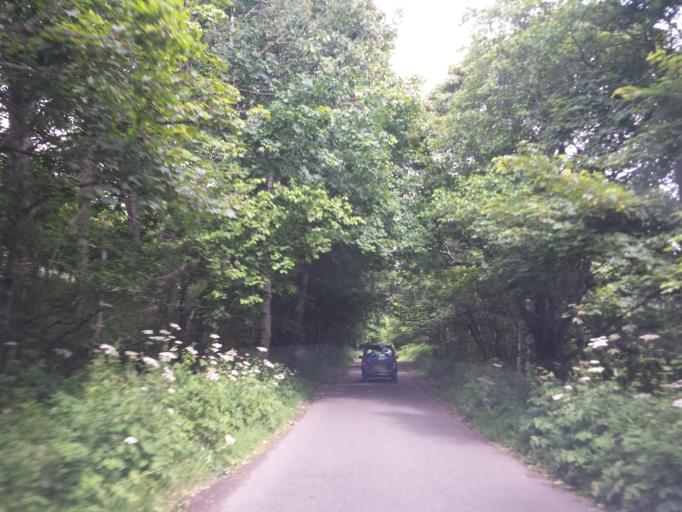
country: GB
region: Scotland
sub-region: Highland
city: Fortrose
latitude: 57.4764
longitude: -4.0729
